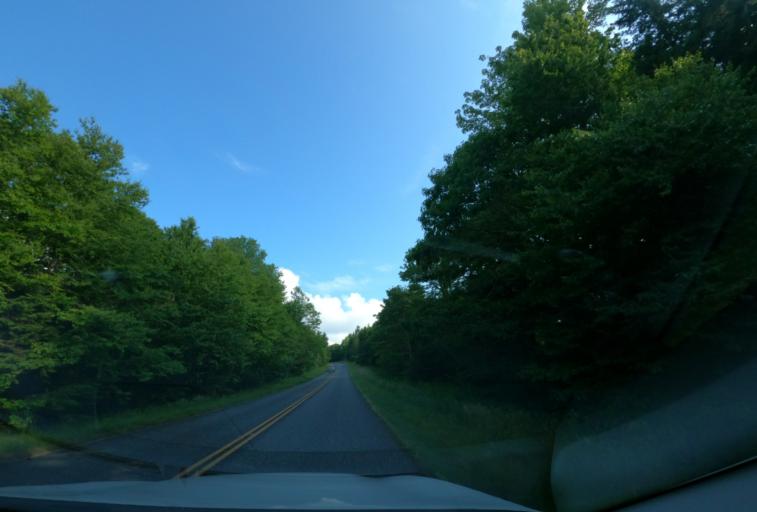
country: US
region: North Carolina
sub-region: Haywood County
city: Hazelwood
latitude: 35.3056
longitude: -82.9430
